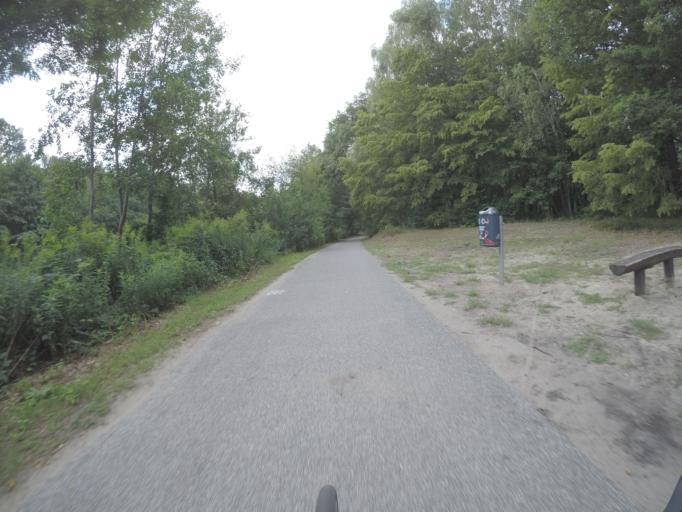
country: DE
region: Brandenburg
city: Hennigsdorf
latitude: 52.6139
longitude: 13.1913
